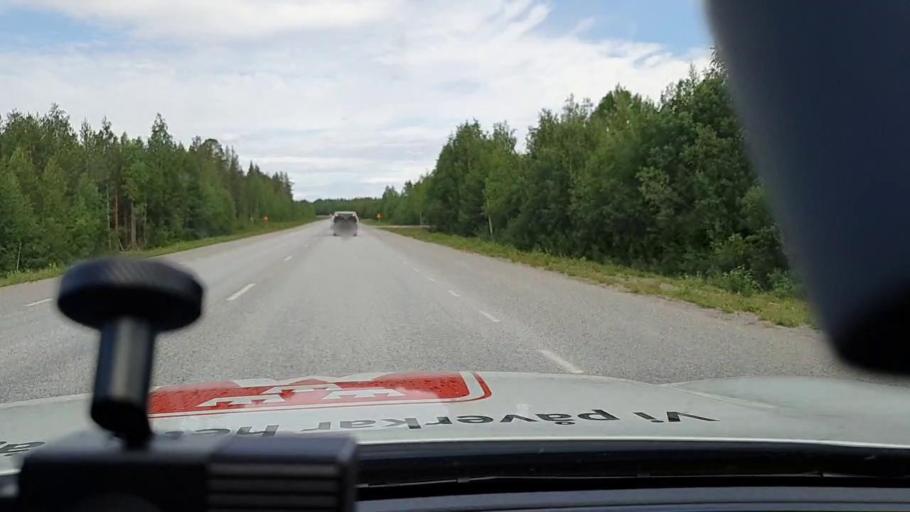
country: SE
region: Norrbotten
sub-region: Jokkmokks Kommun
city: Jokkmokk
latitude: 66.5044
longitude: 20.2515
